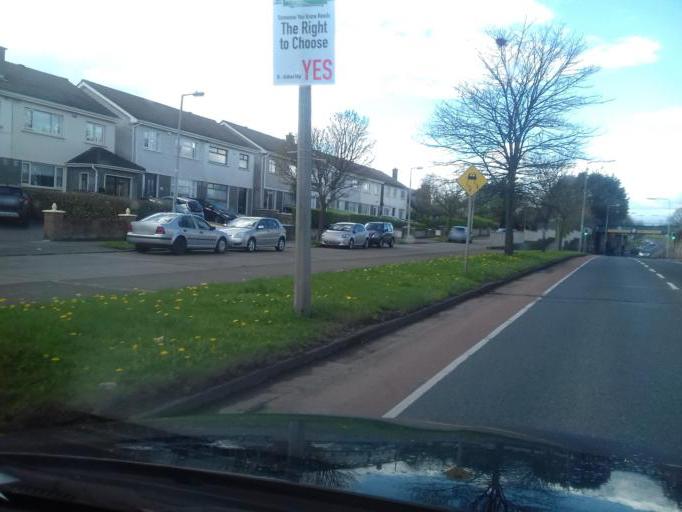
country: IE
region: Leinster
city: Donaghmede
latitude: 53.3899
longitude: -6.1551
